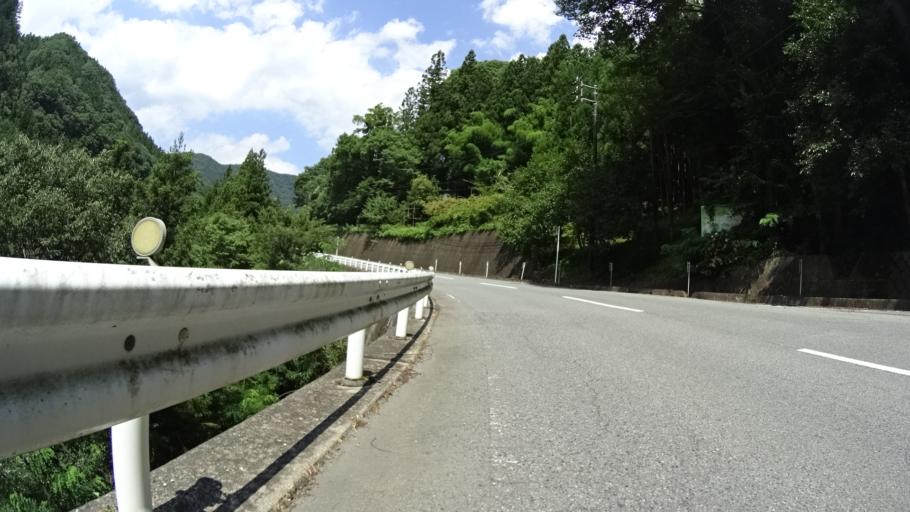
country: JP
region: Gunma
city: Tomioka
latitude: 36.0791
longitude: 138.7790
